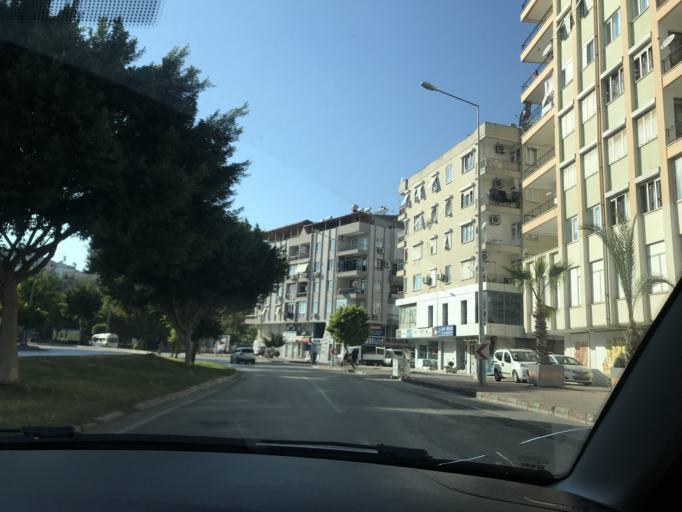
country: TR
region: Antalya
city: Antalya
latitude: 36.9037
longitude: 30.7032
